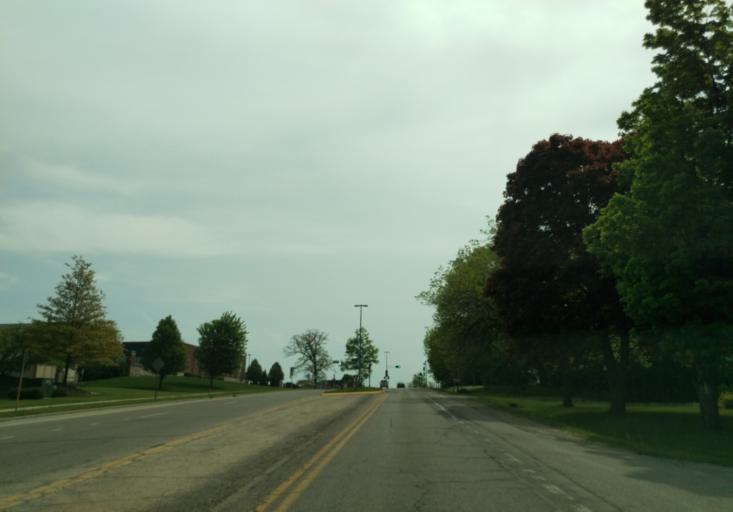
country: US
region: Wisconsin
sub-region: Dane County
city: Monona
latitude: 43.0845
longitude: -89.2815
